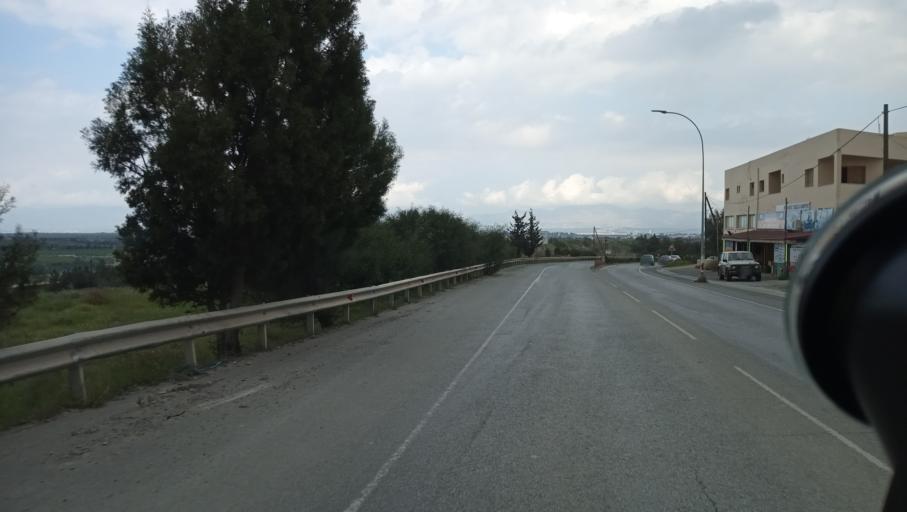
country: CY
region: Lefkosia
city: Kato Deftera
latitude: 35.1225
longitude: 33.2902
